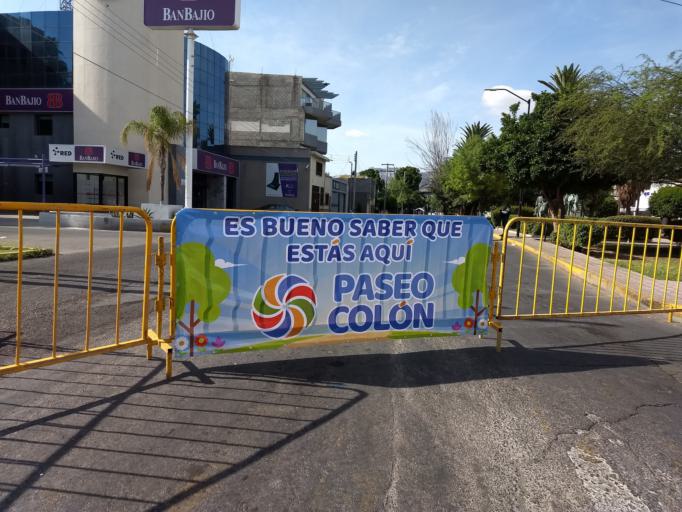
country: MX
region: Coahuila
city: Torreon
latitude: 25.5471
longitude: -103.4485
